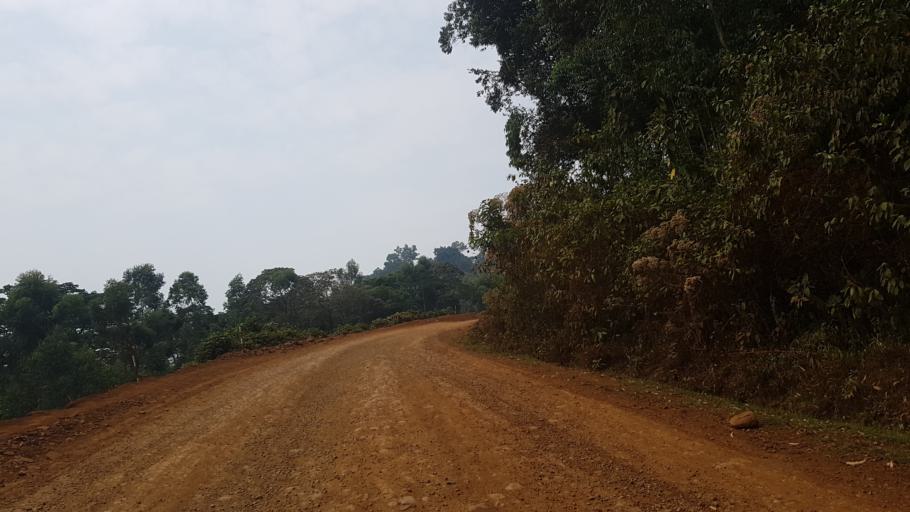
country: ET
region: Oromiya
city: Gore
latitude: 7.8245
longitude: 35.4619
